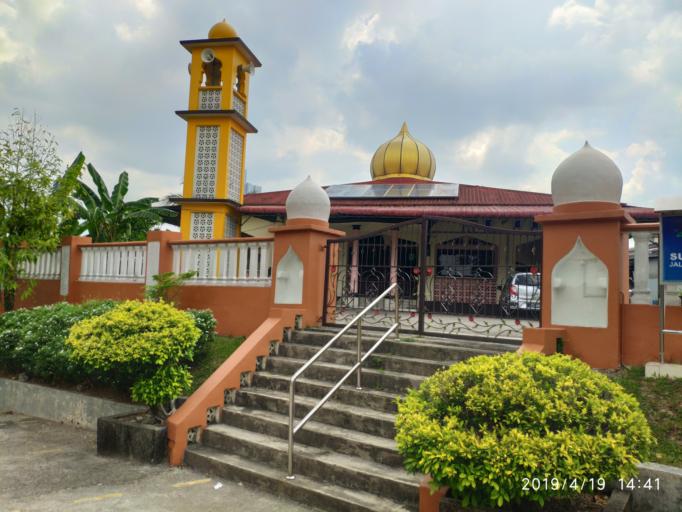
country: MY
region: Johor
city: Johor Bahru
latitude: 1.4742
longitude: 103.7770
